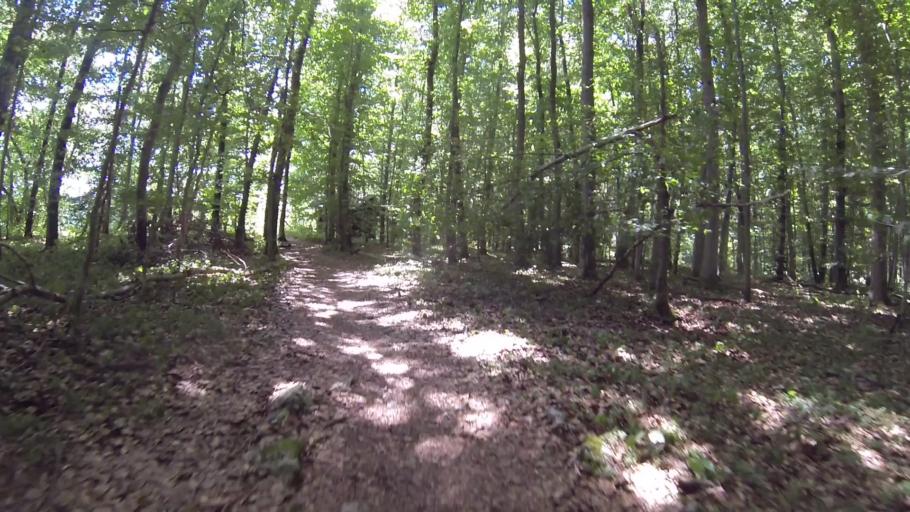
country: DE
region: Baden-Wuerttemberg
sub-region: Regierungsbezirk Stuttgart
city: Herbrechtingen
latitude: 48.6055
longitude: 10.1709
